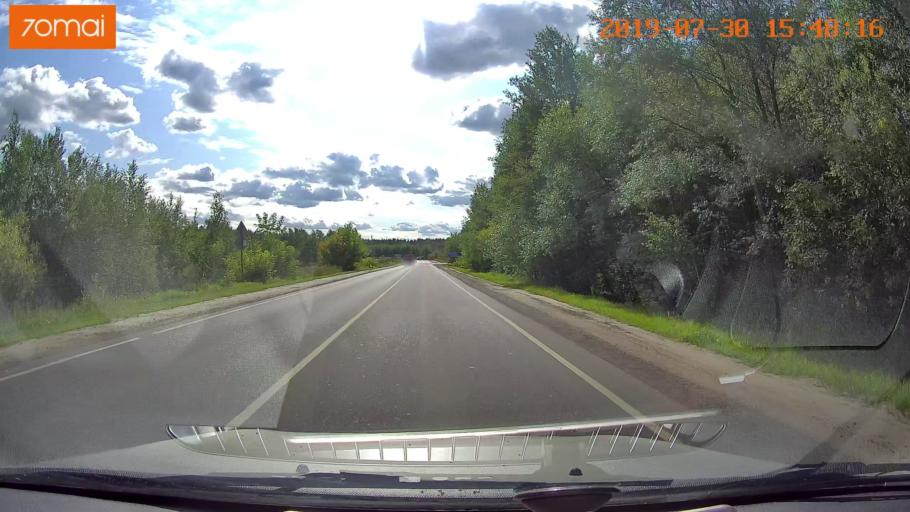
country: RU
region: Moskovskaya
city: Voskresensk
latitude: 55.3426
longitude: 38.6822
